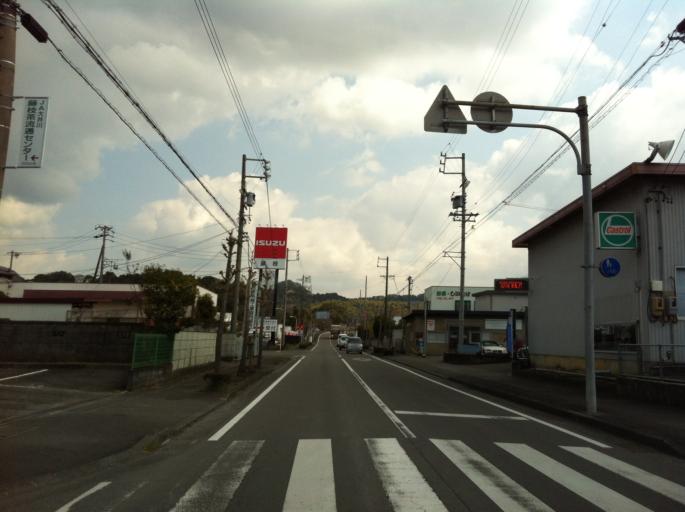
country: JP
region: Shizuoka
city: Fujieda
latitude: 34.8718
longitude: 138.2312
